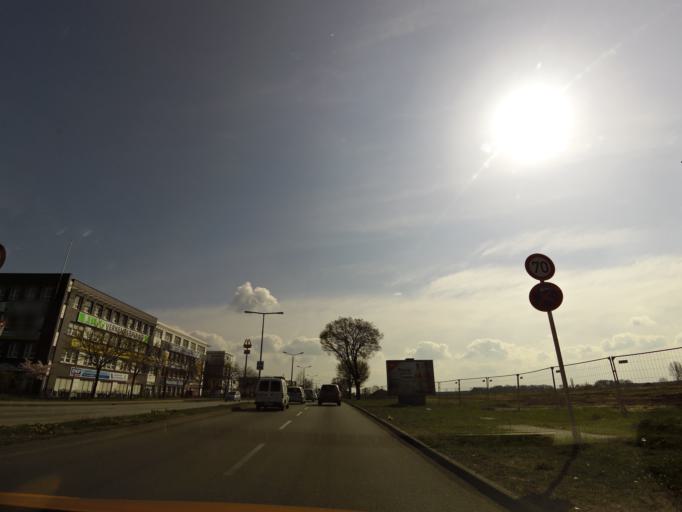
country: DE
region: Berlin
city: Mahlsdorf
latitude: 52.5042
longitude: 13.6208
